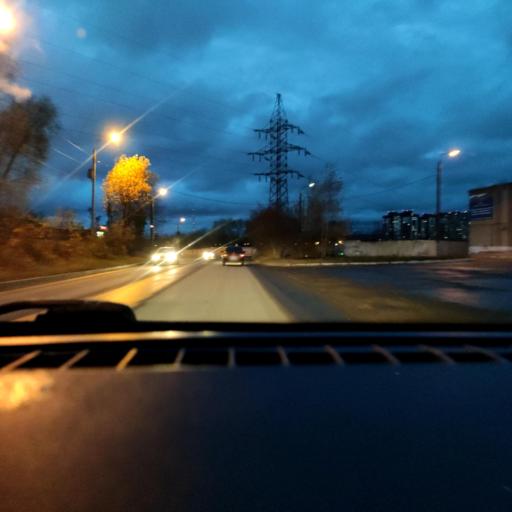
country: RU
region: Perm
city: Perm
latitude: 57.9797
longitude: 56.2702
